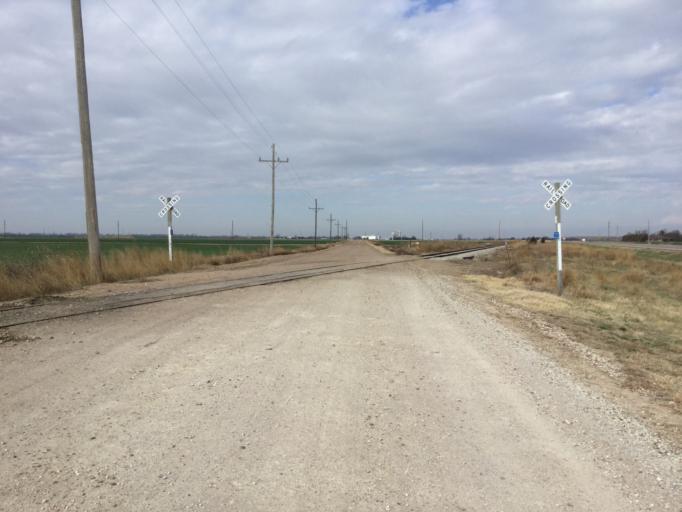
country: US
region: Kansas
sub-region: Barton County
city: Ellinwood
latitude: 38.3621
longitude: -98.6205
